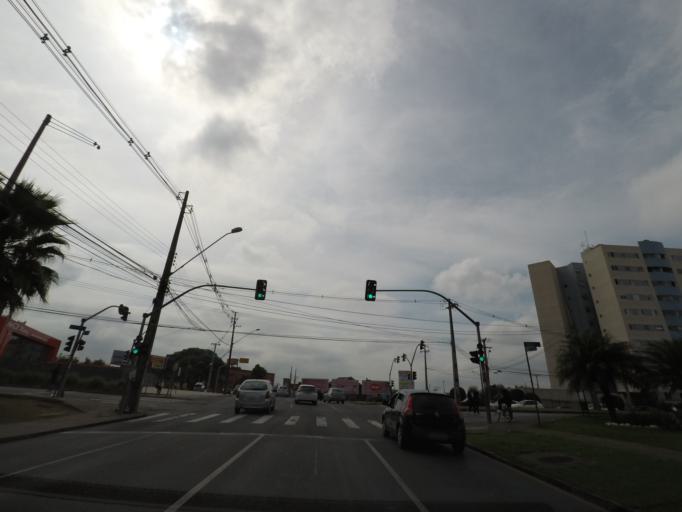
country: BR
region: Parana
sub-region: Curitiba
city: Curitiba
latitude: -25.4774
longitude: -49.2891
